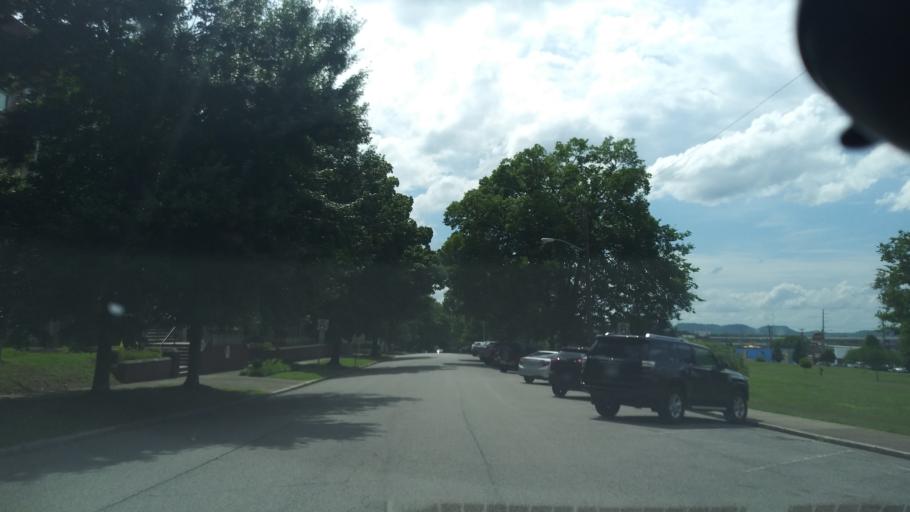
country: US
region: Tennessee
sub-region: Davidson County
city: Belle Meade
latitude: 36.1510
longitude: -86.8449
